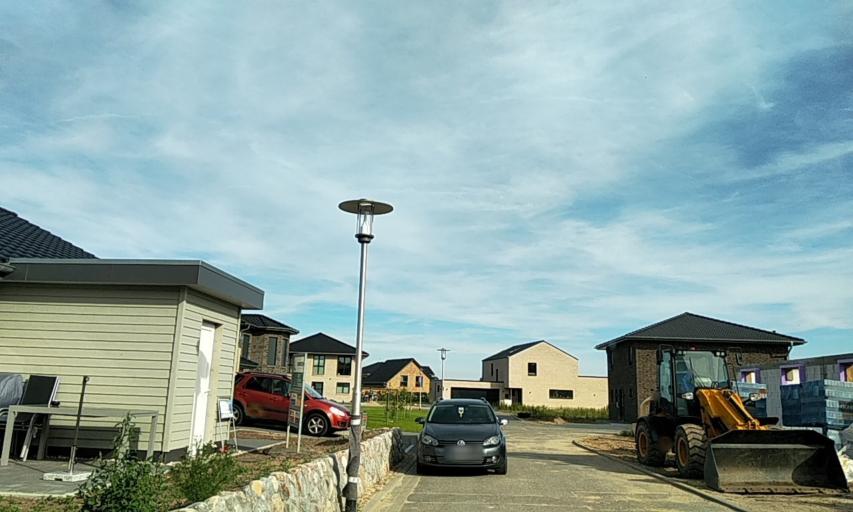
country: DE
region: Schleswig-Holstein
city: Schleswig
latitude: 54.5379
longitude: 9.5669
